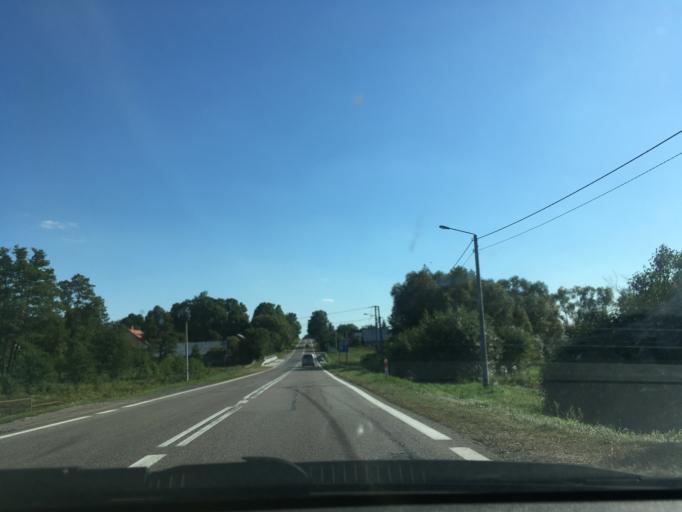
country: PL
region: Podlasie
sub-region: Powiat sokolski
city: Suchowola
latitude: 53.4913
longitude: 23.0951
